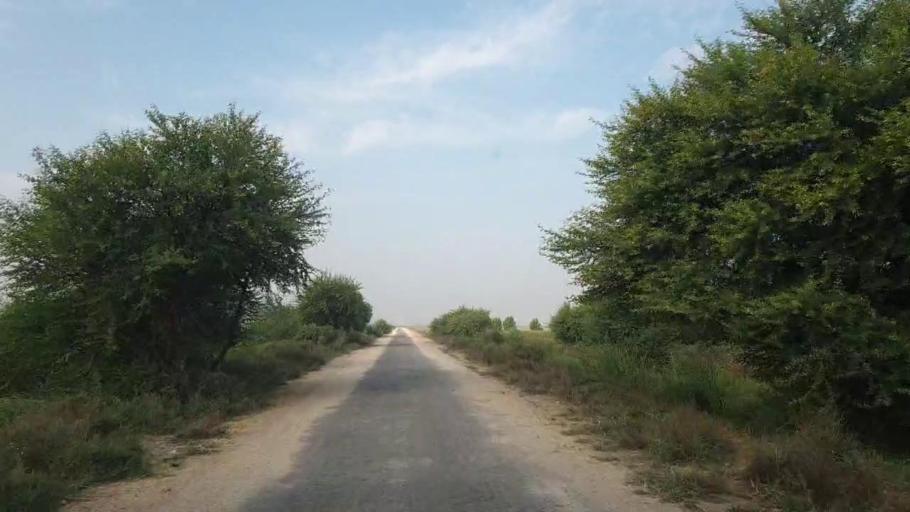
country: PK
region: Sindh
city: Tando Bago
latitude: 24.8445
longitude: 68.9922
